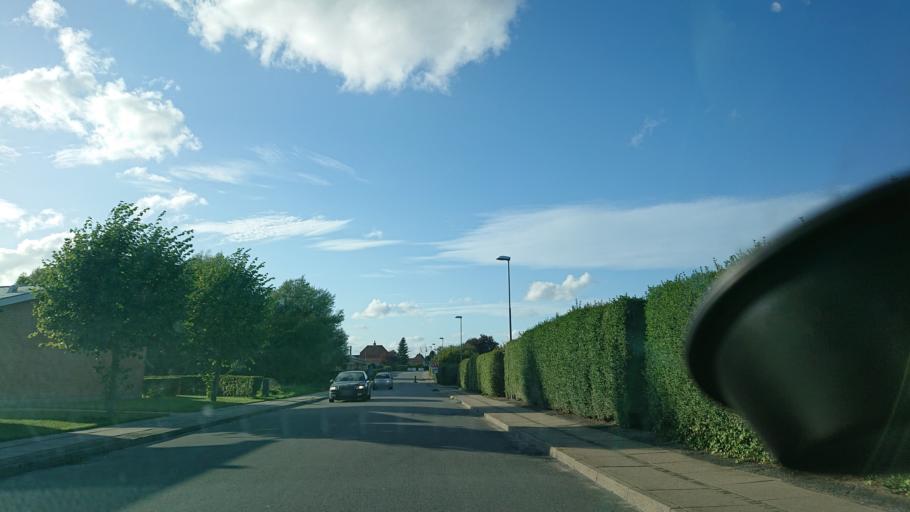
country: DK
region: South Denmark
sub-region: Nyborg Kommune
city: Nyborg
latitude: 55.3082
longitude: 10.7756
